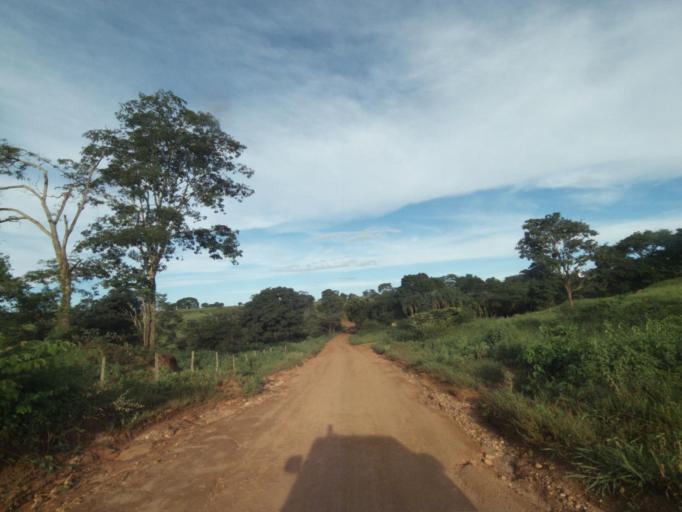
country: BR
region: Goias
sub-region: Jaragua
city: Jaragua
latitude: -15.8895
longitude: -49.4760
